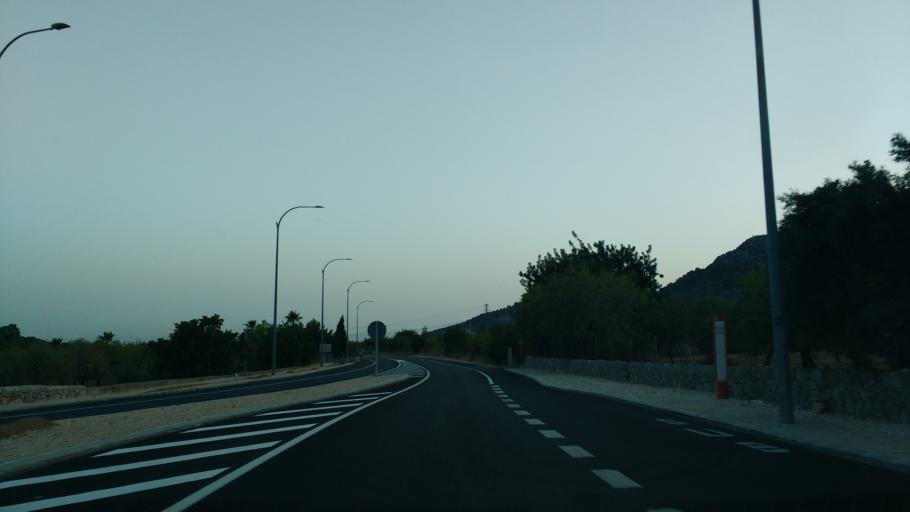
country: ES
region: Balearic Islands
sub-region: Illes Balears
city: Bunyola
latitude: 39.6954
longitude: 2.6871
